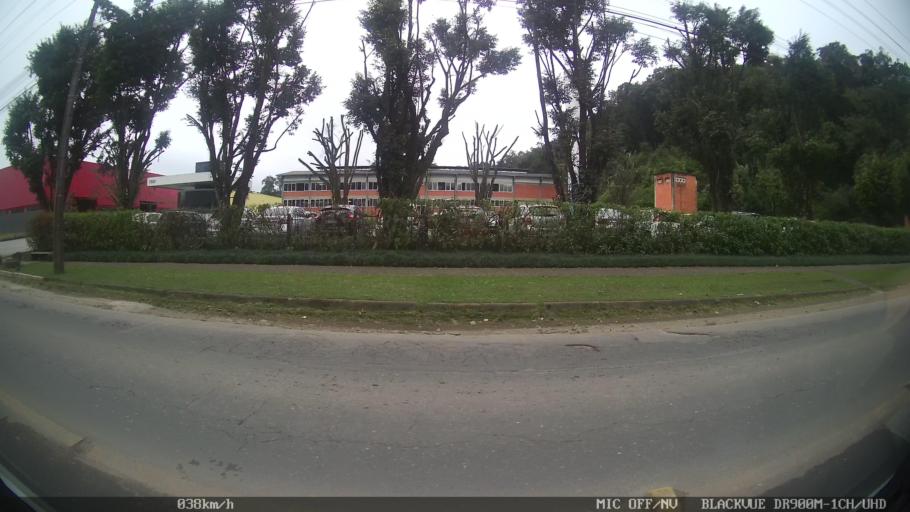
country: BR
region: Santa Catarina
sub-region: Joinville
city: Joinville
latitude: -26.2484
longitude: -48.8771
